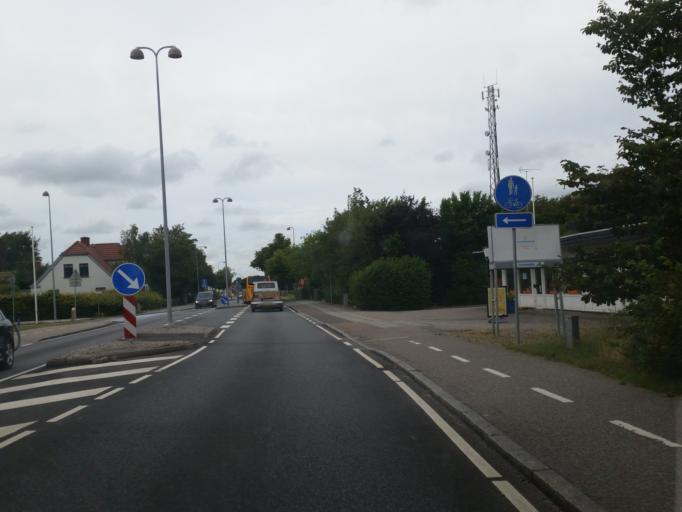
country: DK
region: South Denmark
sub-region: Esbjerg Kommune
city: Ribe
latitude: 55.2735
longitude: 8.7279
